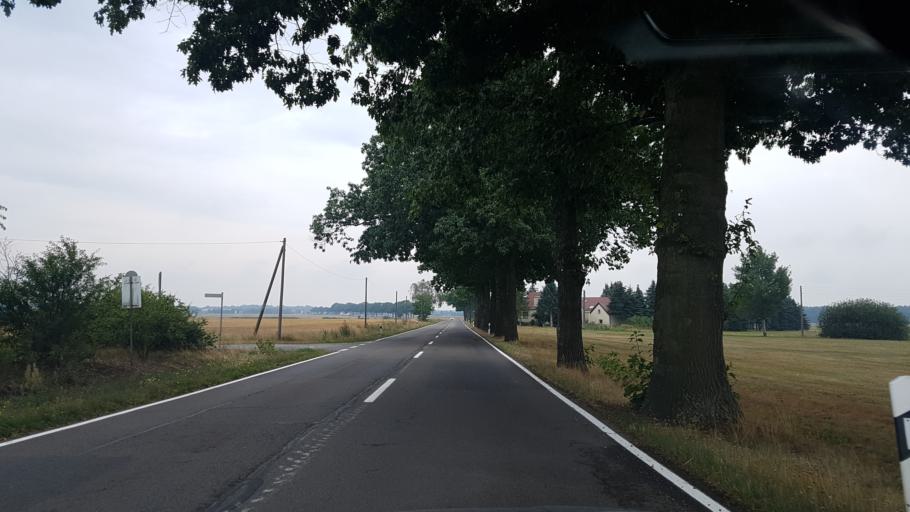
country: DE
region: Brandenburg
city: Grunewald
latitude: 51.4004
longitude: 14.0041
